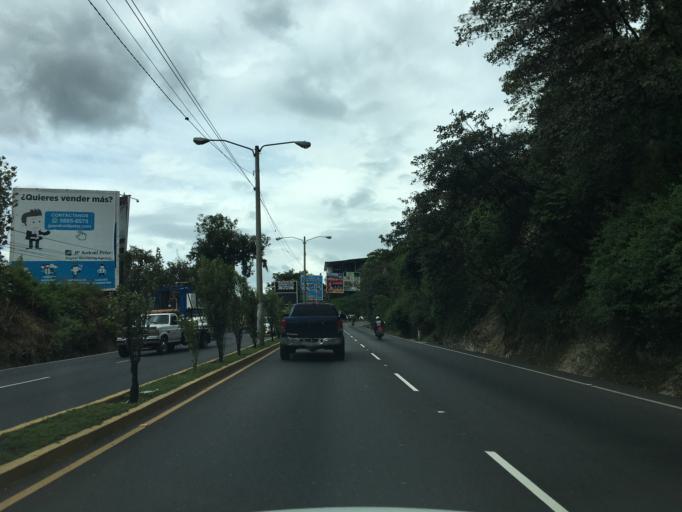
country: GT
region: Guatemala
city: Mixco
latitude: 14.5940
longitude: -90.5708
